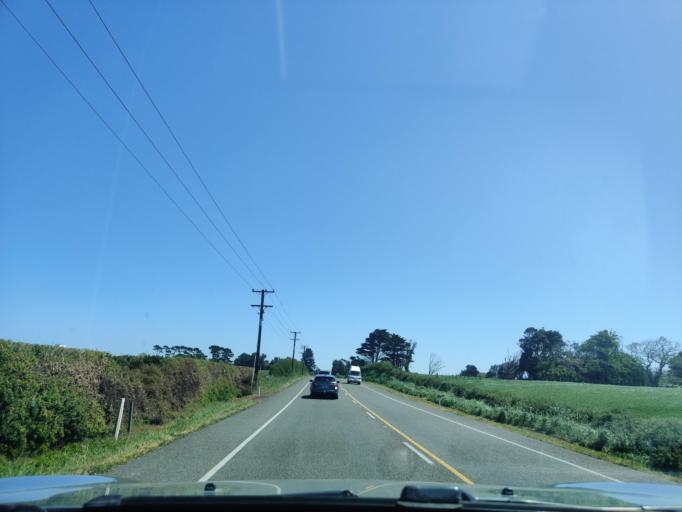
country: NZ
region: Taranaki
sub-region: South Taranaki District
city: Hawera
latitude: -39.6083
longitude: 174.3206
